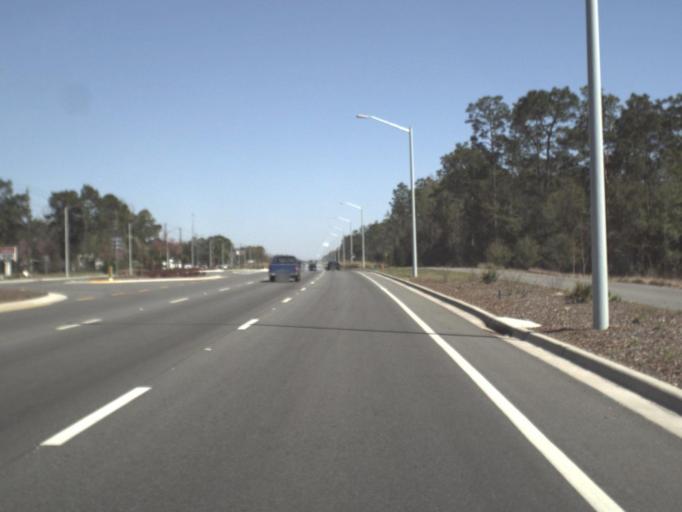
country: US
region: Florida
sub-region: Leon County
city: Tallahassee
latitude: 30.3757
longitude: -84.2880
